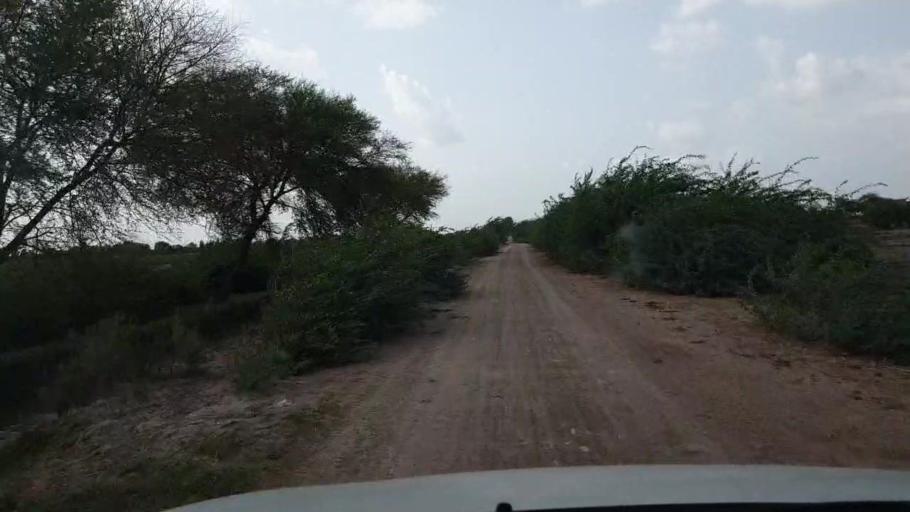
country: PK
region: Sindh
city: Kario
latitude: 24.7258
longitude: 68.6368
